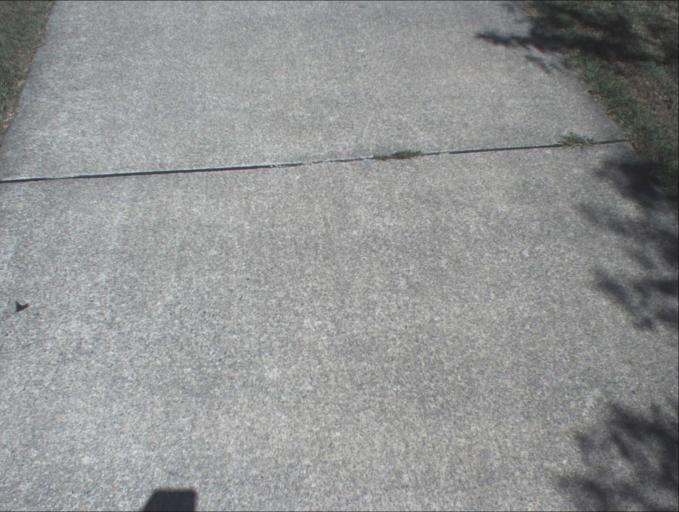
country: AU
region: Queensland
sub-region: Logan
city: Windaroo
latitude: -27.7366
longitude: 153.1985
